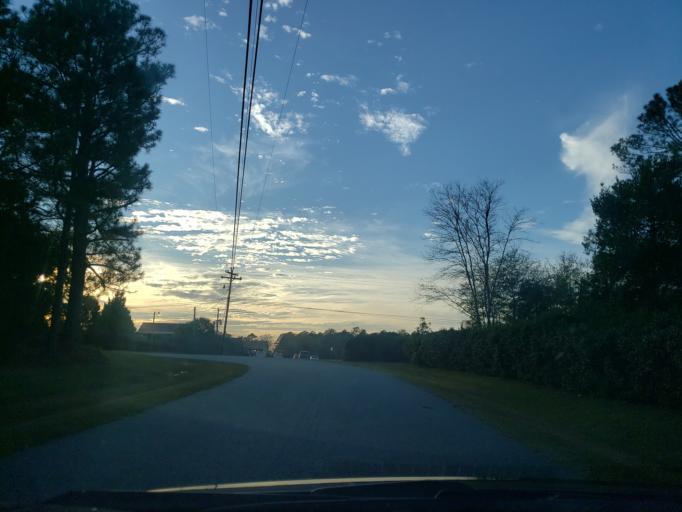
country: US
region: Georgia
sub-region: Tift County
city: Unionville
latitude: 31.4478
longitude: -83.5818
